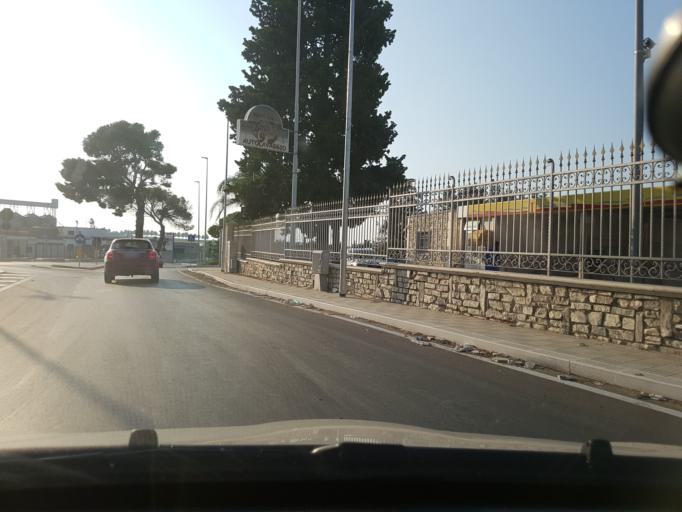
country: IT
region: Apulia
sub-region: Provincia di Foggia
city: Cerignola
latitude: 41.2672
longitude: 15.8856
